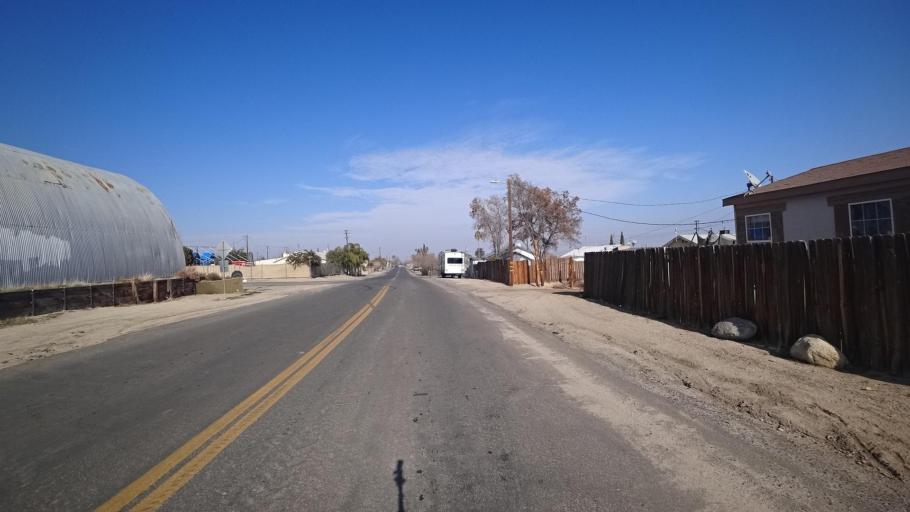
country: US
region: California
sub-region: Kern County
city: Taft Heights
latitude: 35.1325
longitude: -119.4648
